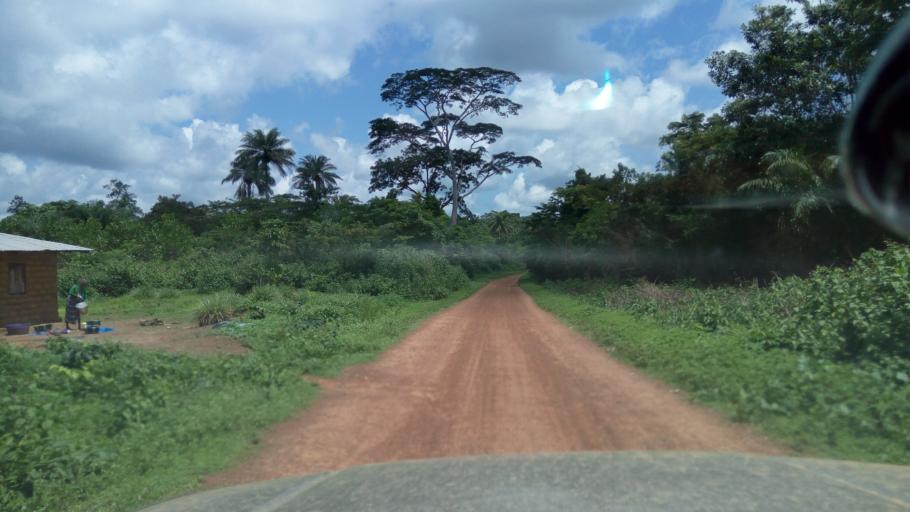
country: SL
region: Southern Province
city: Zimmi
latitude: 7.2722
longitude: -11.2708
